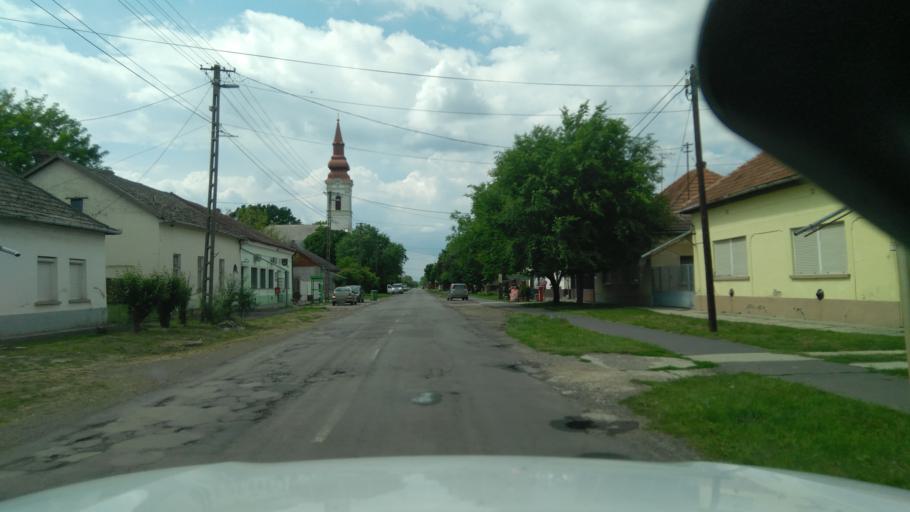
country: HU
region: Bekes
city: Magyarbanhegyes
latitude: 46.4555
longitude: 20.9663
